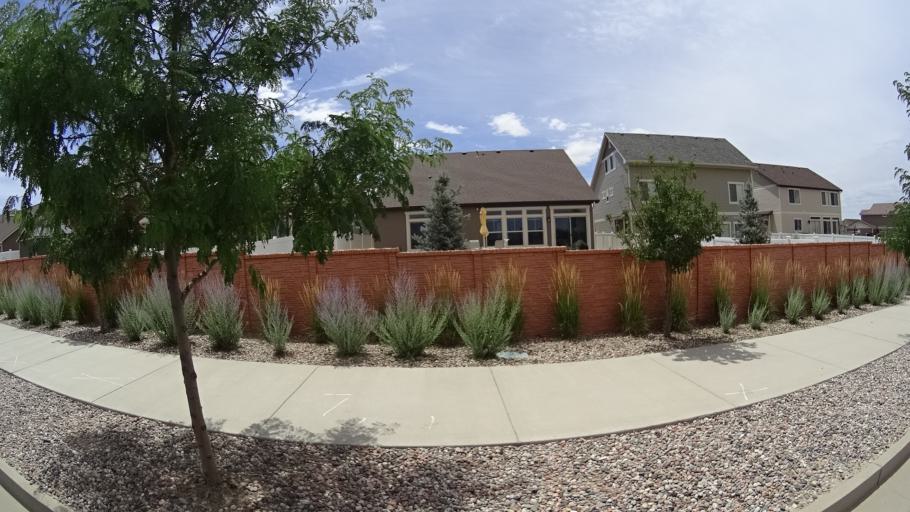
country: US
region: Colorado
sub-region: El Paso County
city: Fountain
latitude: 38.6938
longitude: -104.6778
